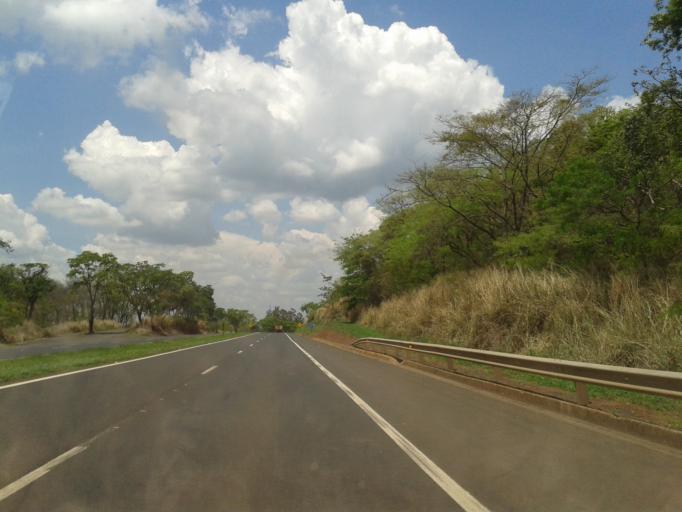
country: BR
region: Minas Gerais
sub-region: Araguari
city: Araguari
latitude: -18.7285
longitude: -48.2070
